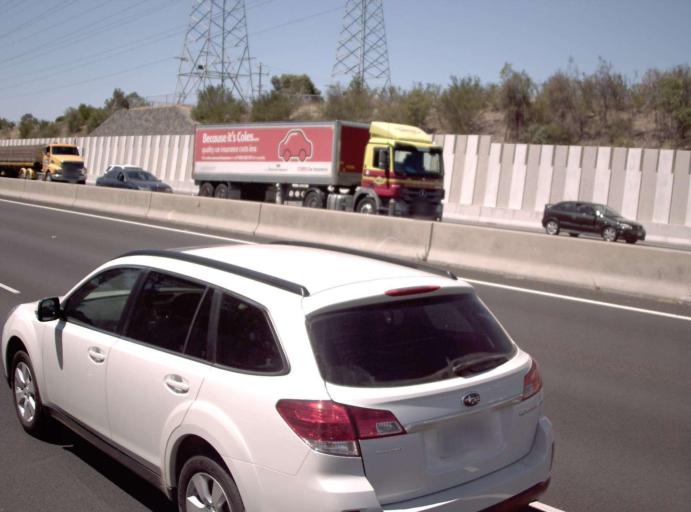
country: AU
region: Victoria
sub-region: Moreland
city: Glenroy
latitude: -37.6942
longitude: 144.9236
